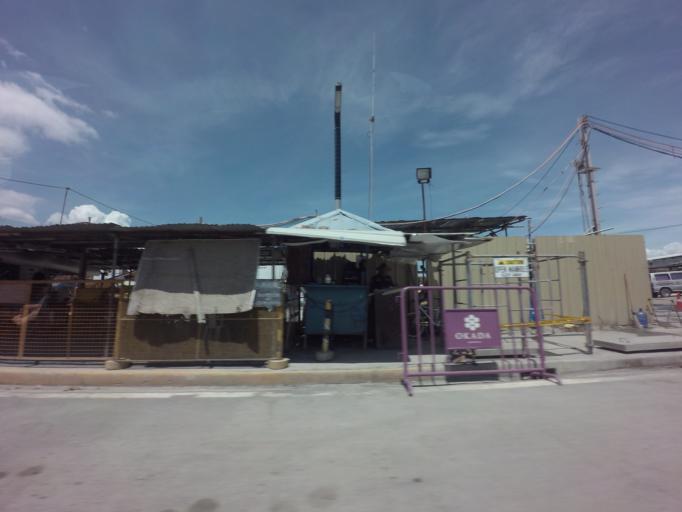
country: PH
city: Sambayanihan People's Village
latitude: 14.5123
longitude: 120.9828
